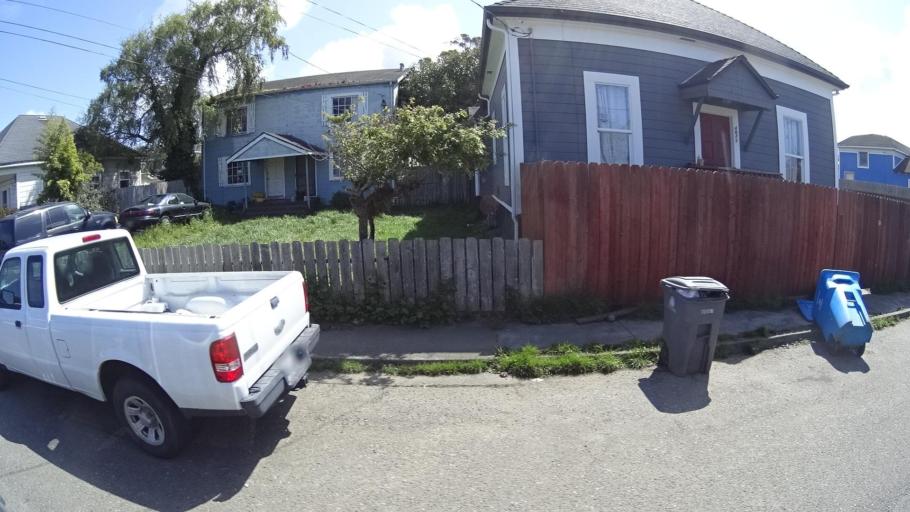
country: US
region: California
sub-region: Humboldt County
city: Bayview
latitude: 40.7702
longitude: -124.1820
